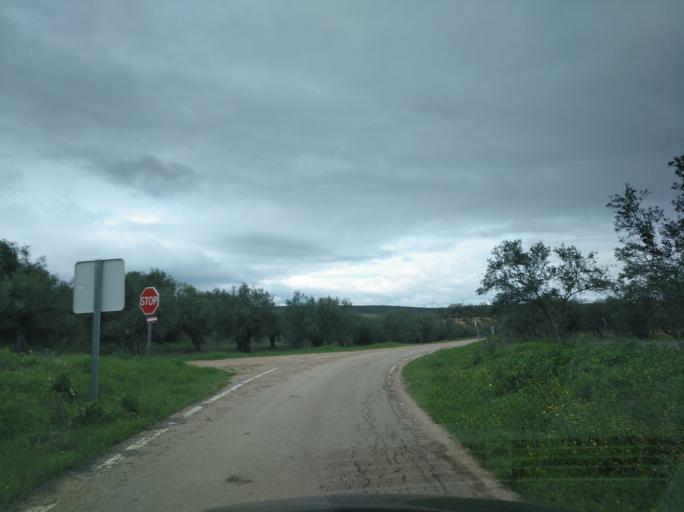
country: PT
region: Portalegre
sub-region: Campo Maior
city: Campo Maior
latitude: 38.9875
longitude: -7.0441
